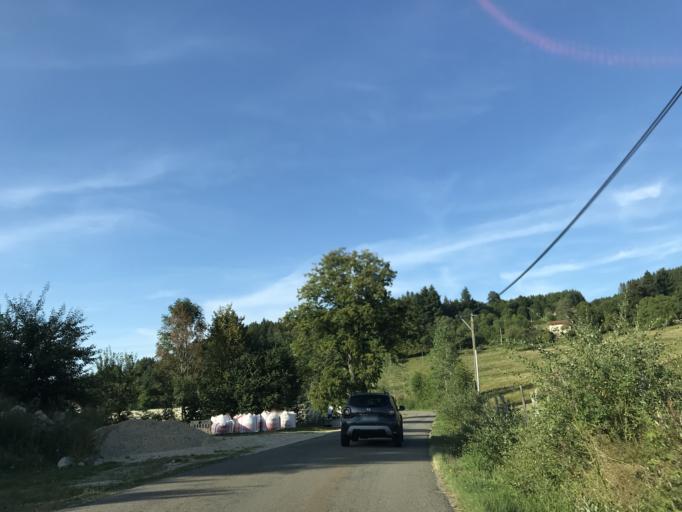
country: FR
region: Auvergne
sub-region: Departement du Puy-de-Dome
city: Job
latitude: 45.7023
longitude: 3.7214
